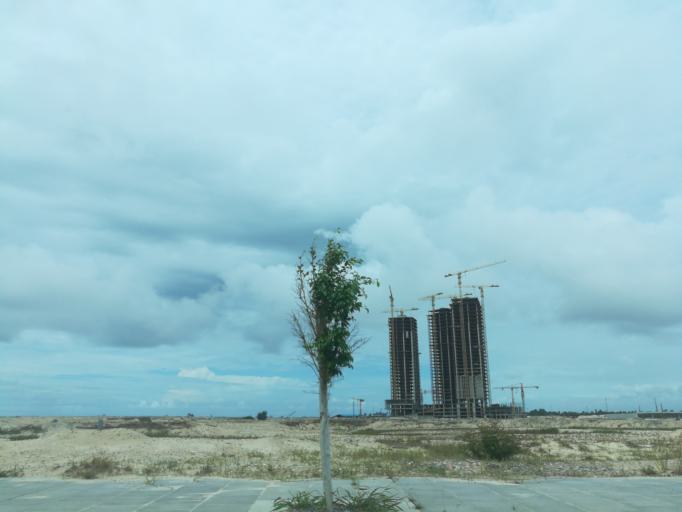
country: NG
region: Lagos
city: Lagos
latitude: 6.4037
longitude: 3.4124
